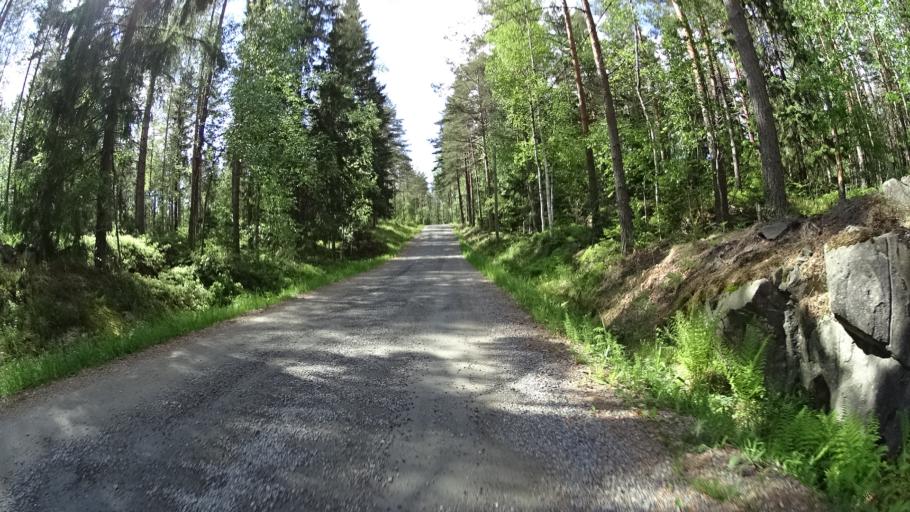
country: FI
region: Uusimaa
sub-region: Raaseporin
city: Pohja
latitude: 60.1851
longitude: 23.5801
